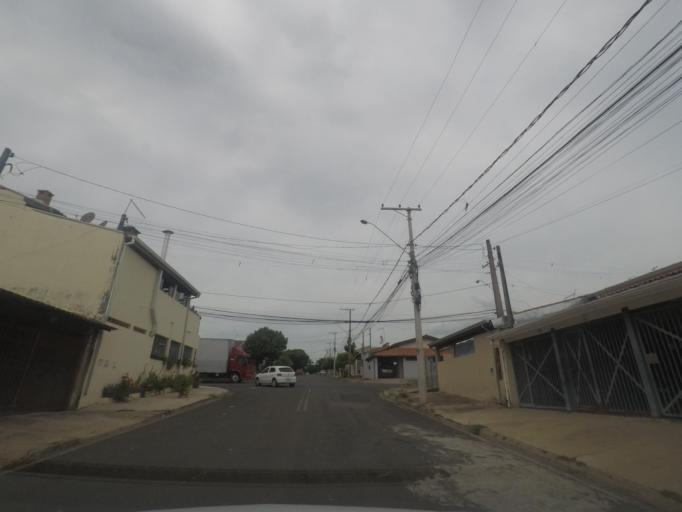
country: BR
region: Sao Paulo
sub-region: Nova Odessa
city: Nova Odessa
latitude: -22.7984
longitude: -47.2823
